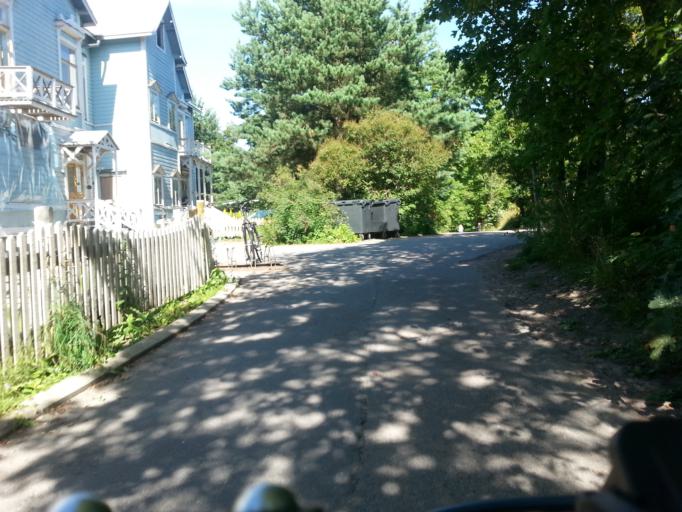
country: FI
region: Uusimaa
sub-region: Helsinki
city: Helsinki
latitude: 60.1814
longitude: 24.9372
